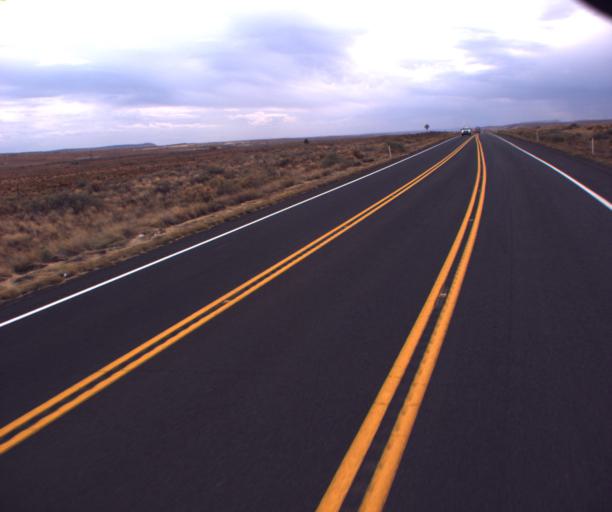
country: US
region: Arizona
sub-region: Coconino County
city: Kaibito
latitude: 36.3904
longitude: -110.8809
